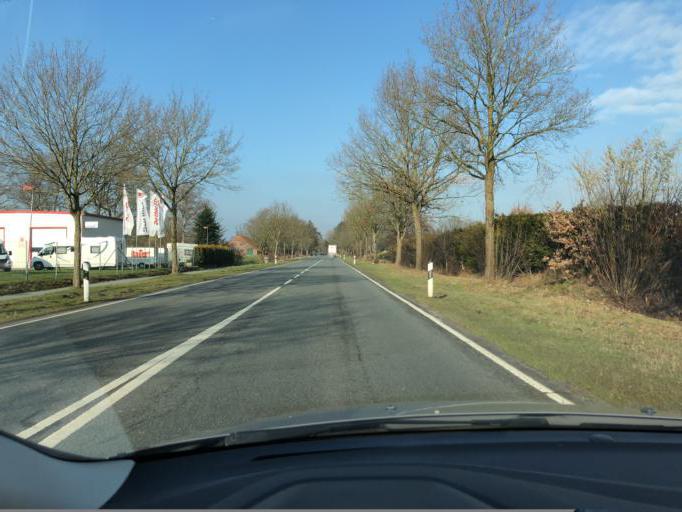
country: DE
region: Lower Saxony
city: Westerstede
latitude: 53.2876
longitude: 7.8925
